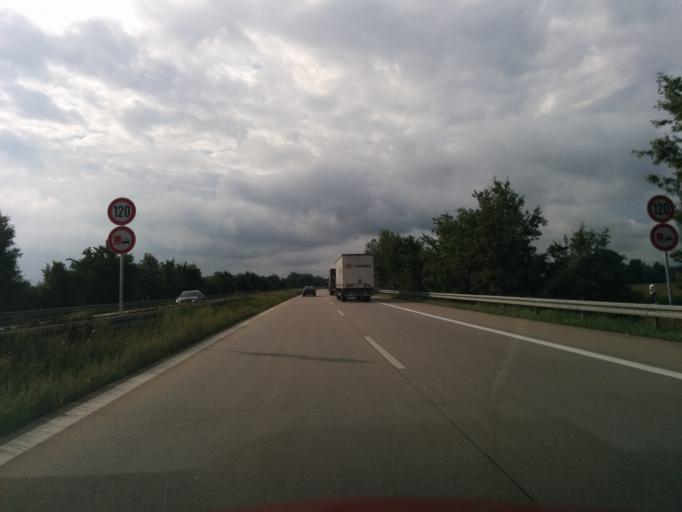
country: DE
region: Bavaria
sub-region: Lower Bavaria
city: Niederwinkling
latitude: 48.8860
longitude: 12.8263
